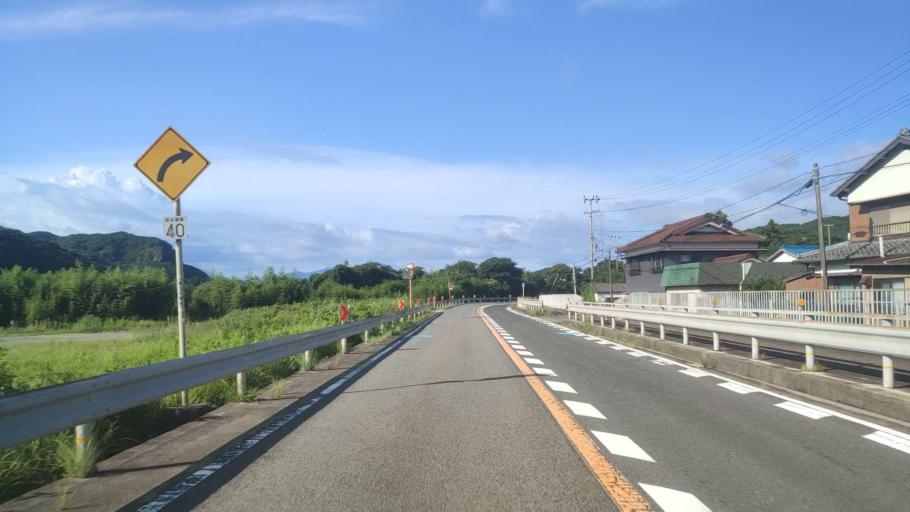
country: JP
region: Wakayama
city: Tanabe
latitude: 33.6633
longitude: 135.3998
